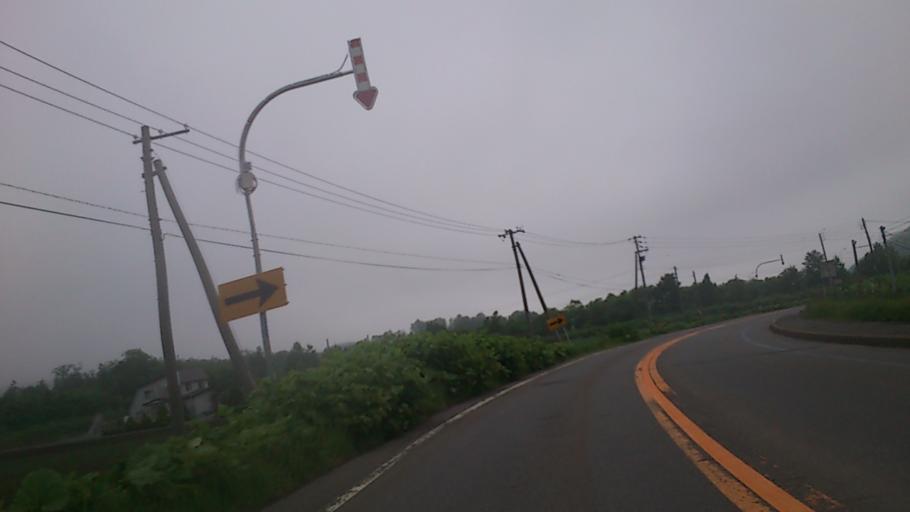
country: JP
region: Hokkaido
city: Niseko Town
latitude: 42.8269
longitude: 140.8905
